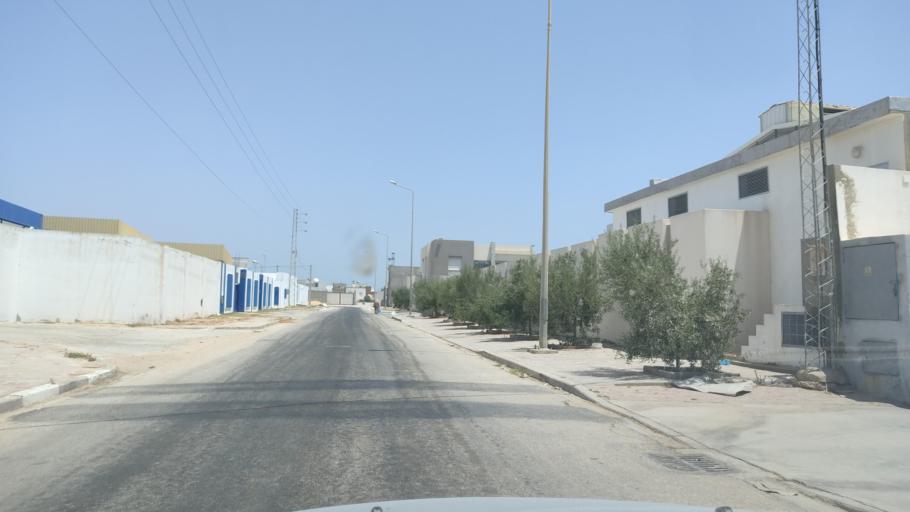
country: TN
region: Safaqis
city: Sfax
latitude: 34.6608
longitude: 10.7002
